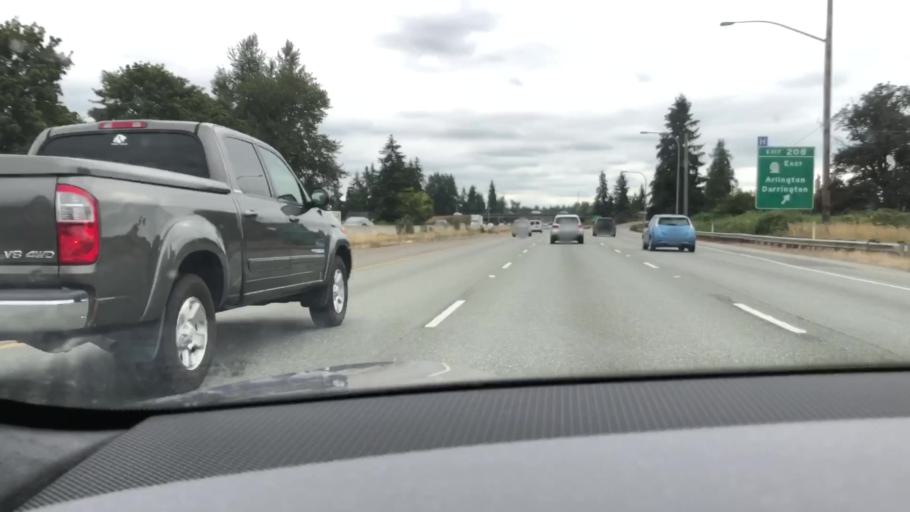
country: US
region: Washington
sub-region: Snohomish County
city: Smokey Point
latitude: 48.1913
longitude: -122.2061
